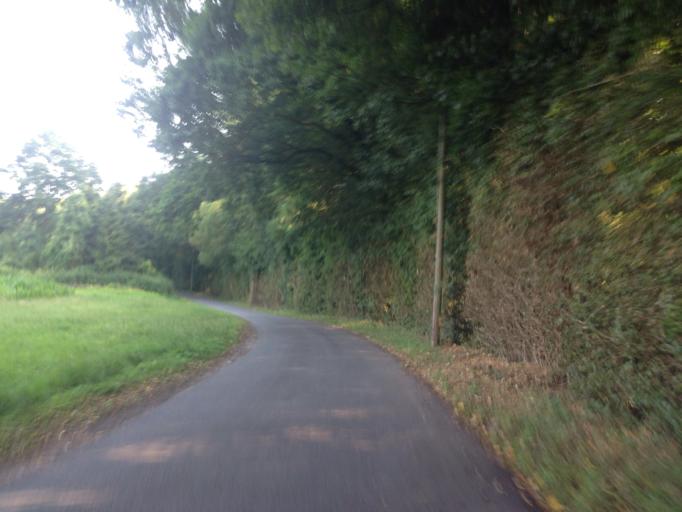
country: DE
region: North Rhine-Westphalia
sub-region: Regierungsbezirk Munster
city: Muenster
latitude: 52.0008
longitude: 7.5781
